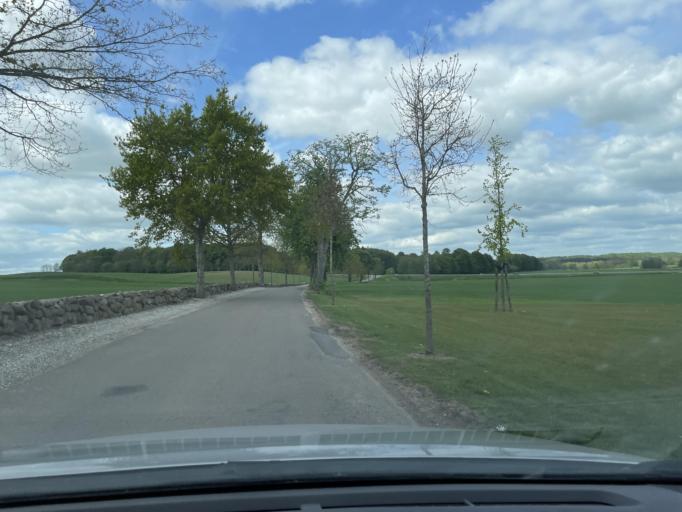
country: DK
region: Central Jutland
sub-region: Odder Kommune
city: Odder
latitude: 55.9124
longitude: 10.1009
